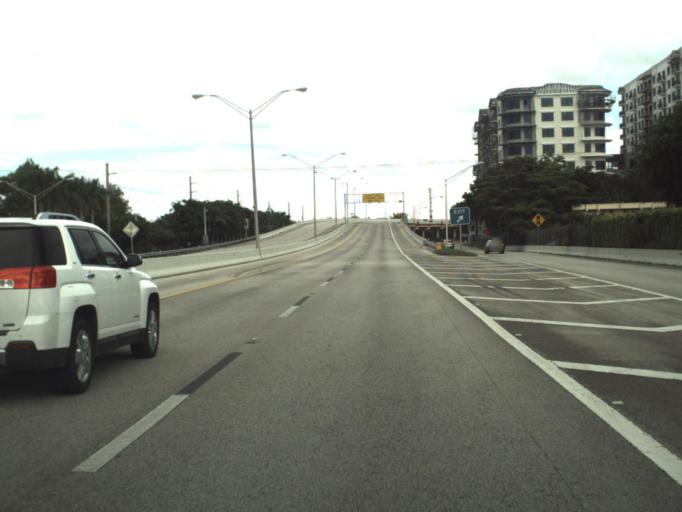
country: US
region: Florida
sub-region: Miami-Dade County
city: Kendall
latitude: 25.6956
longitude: -80.3123
